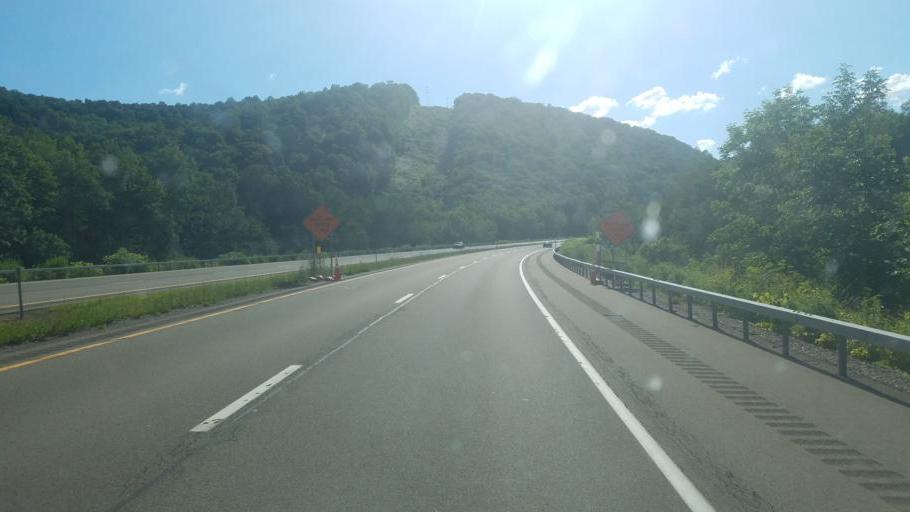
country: US
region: New York
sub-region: Cattaraugus County
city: Salamanca
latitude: 42.1007
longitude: -78.8083
